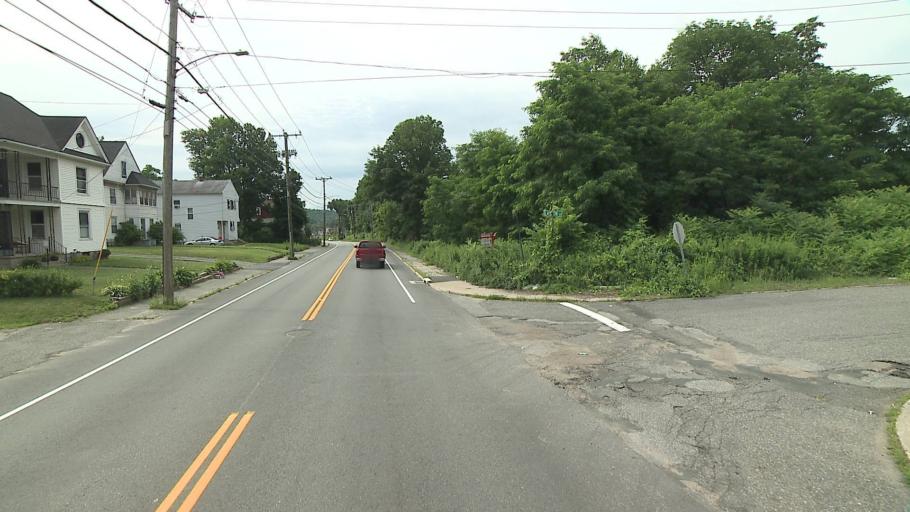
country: US
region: Connecticut
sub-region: Litchfield County
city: Torrington
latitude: 41.7916
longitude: -73.1198
